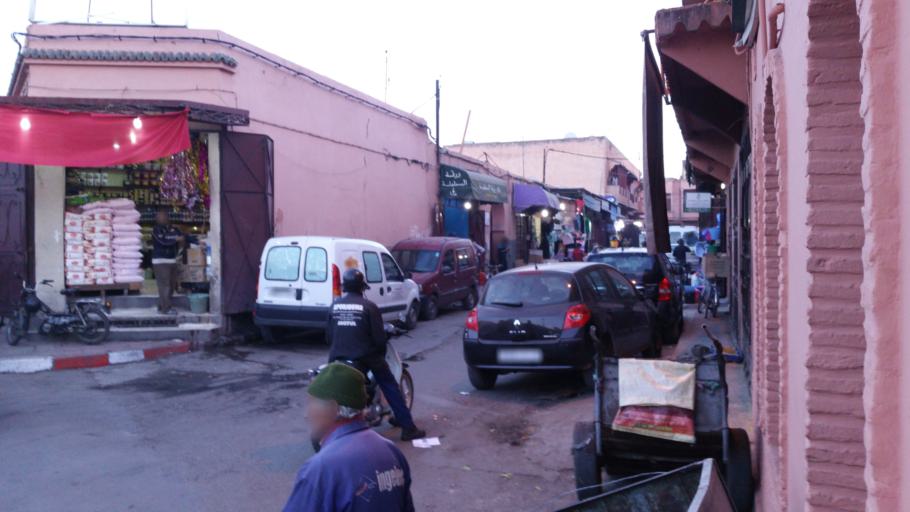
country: MA
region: Marrakech-Tensift-Al Haouz
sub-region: Marrakech
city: Marrakesh
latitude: 31.6204
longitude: -7.9866
